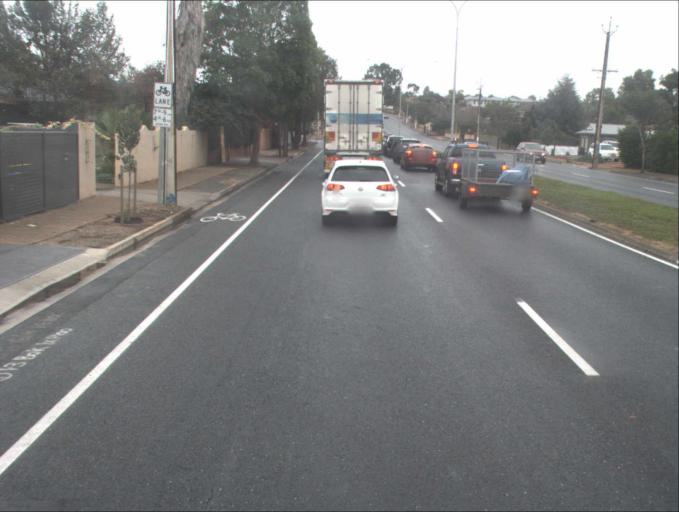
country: AU
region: South Australia
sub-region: Port Adelaide Enfield
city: Klemzig
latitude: -34.8855
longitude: 138.6250
